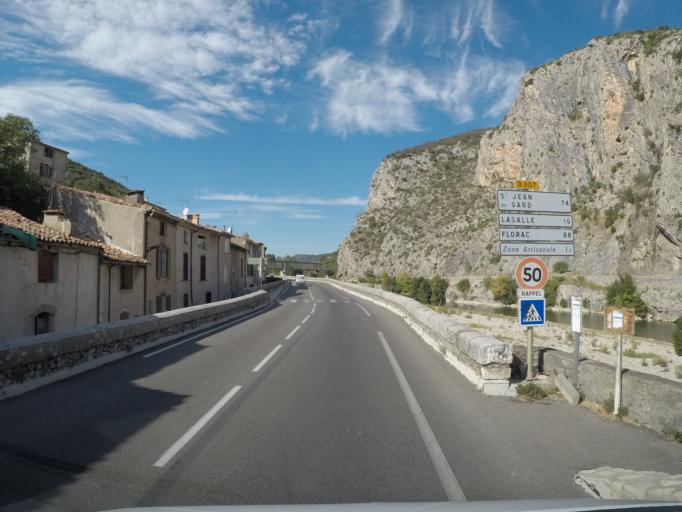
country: FR
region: Languedoc-Roussillon
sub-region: Departement du Gard
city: Anduze
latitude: 44.0576
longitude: 3.9864
